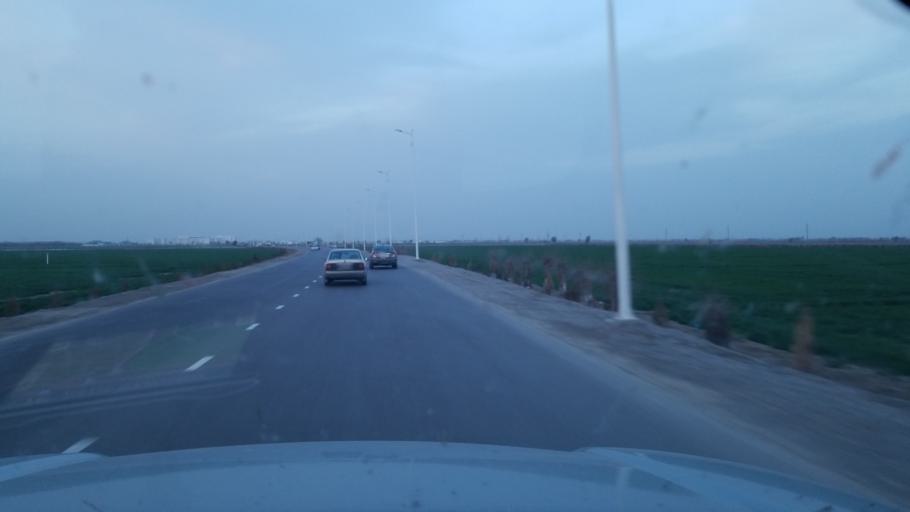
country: TM
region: Lebap
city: Turkmenabat
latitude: 38.9956
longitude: 63.5854
